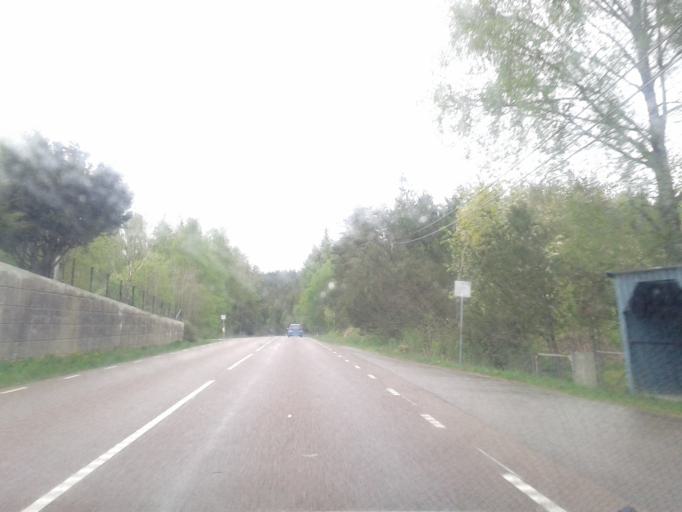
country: SE
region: Vaestra Goetaland
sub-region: Lilla Edets Kommun
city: Lodose
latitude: 58.0763
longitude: 12.1268
